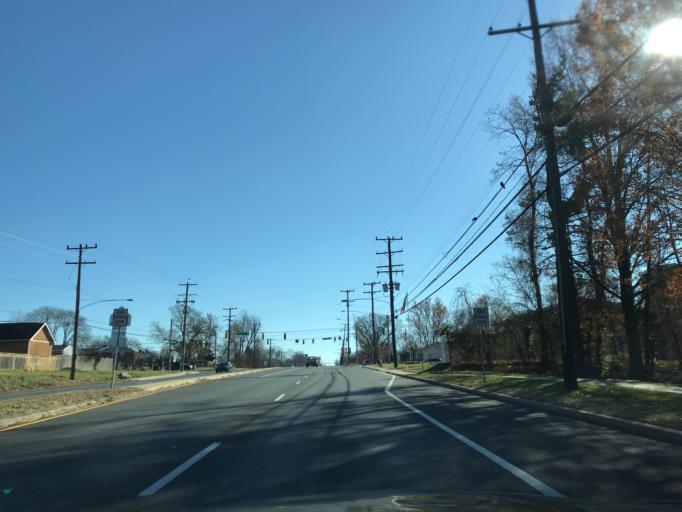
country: US
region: Maryland
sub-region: Montgomery County
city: Aspen Hill
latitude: 39.0622
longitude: -77.0933
